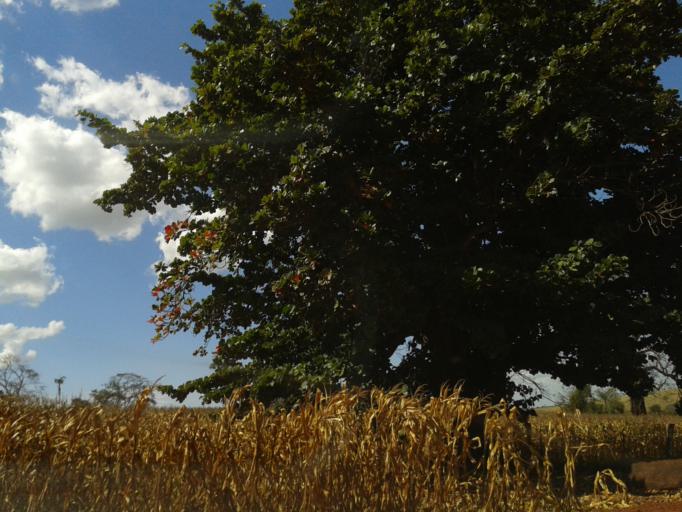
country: BR
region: Minas Gerais
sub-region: Capinopolis
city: Capinopolis
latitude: -18.6282
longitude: -49.4755
